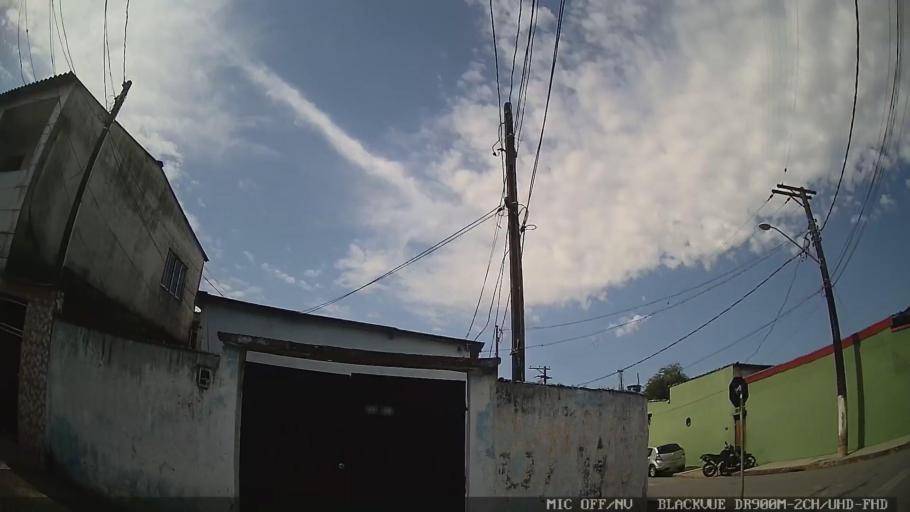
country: BR
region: Sao Paulo
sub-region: Santos
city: Santos
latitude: -23.9461
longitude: -46.2916
